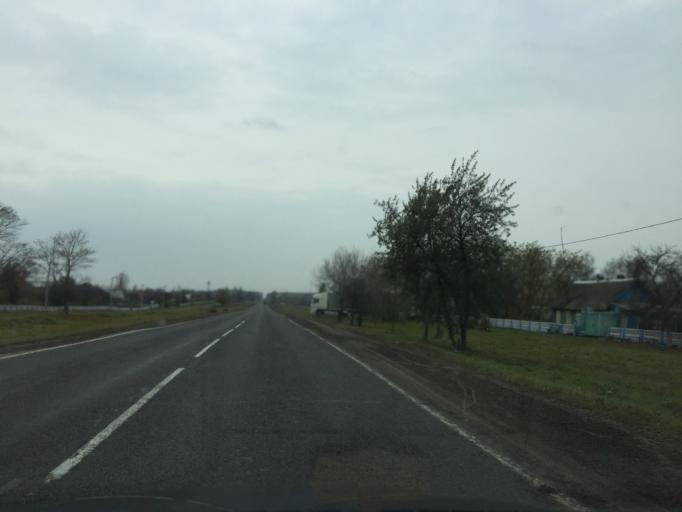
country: BY
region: Gomel
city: Dowsk
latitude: 53.1656
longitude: 30.4790
